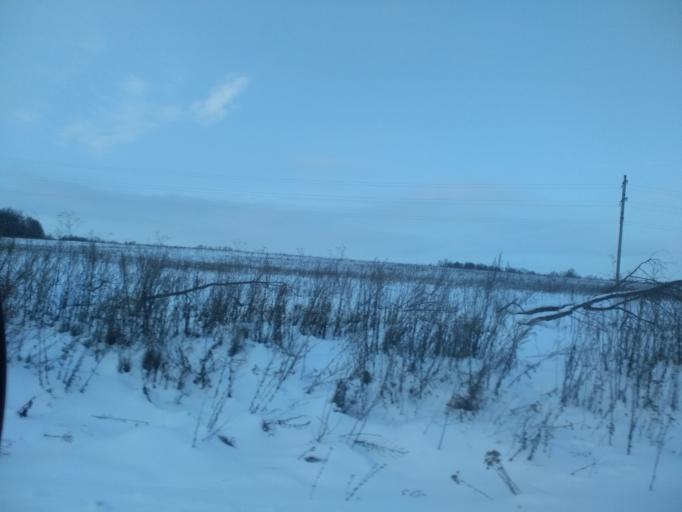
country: RU
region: Bashkortostan
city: Kudeyevskiy
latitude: 54.7152
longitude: 56.6183
